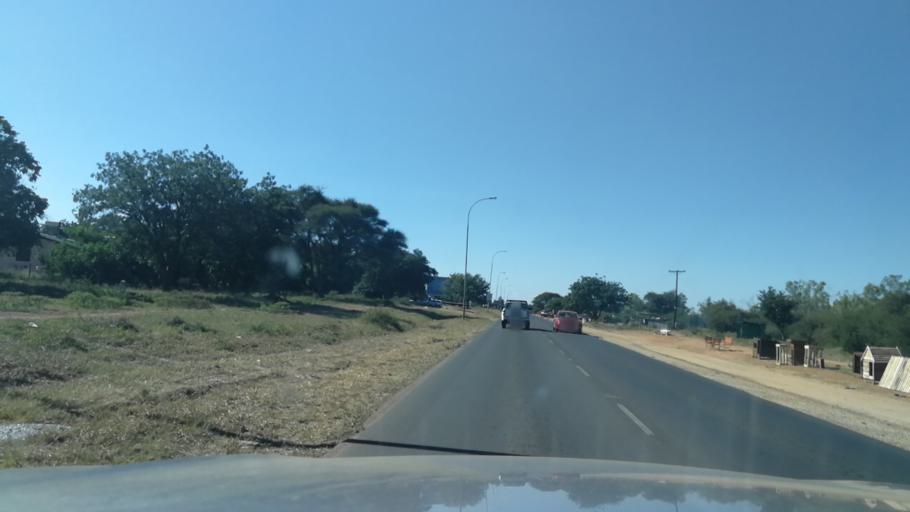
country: BW
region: South East
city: Gaborone
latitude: -24.6951
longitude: 25.8948
